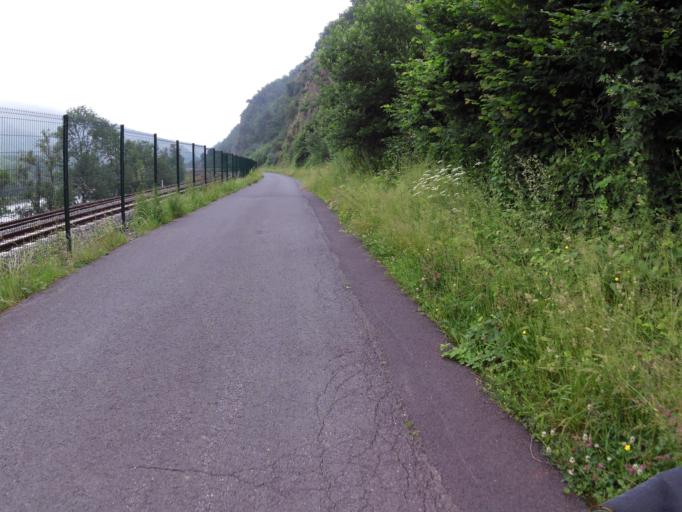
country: FR
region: Champagne-Ardenne
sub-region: Departement des Ardennes
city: Revin
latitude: 49.9478
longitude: 4.6535
